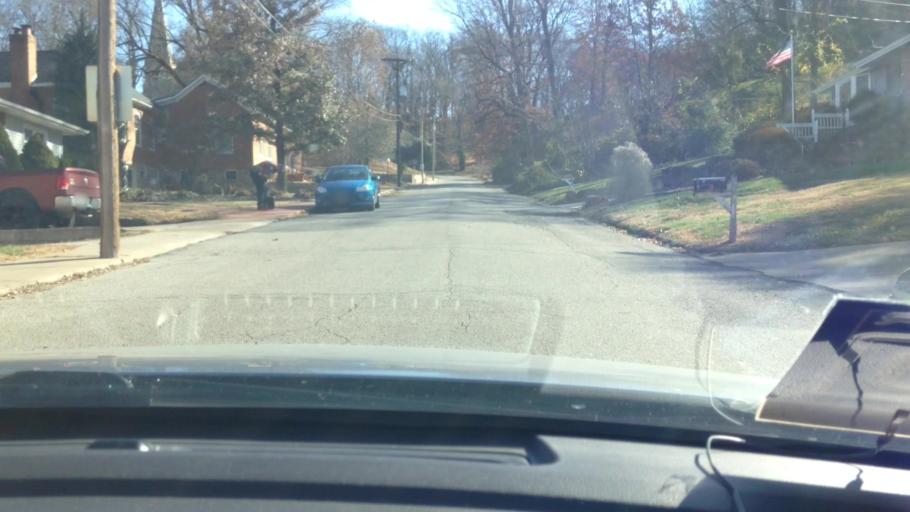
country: US
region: Missouri
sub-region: Platte County
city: Weston
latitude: 39.4098
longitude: -94.9011
